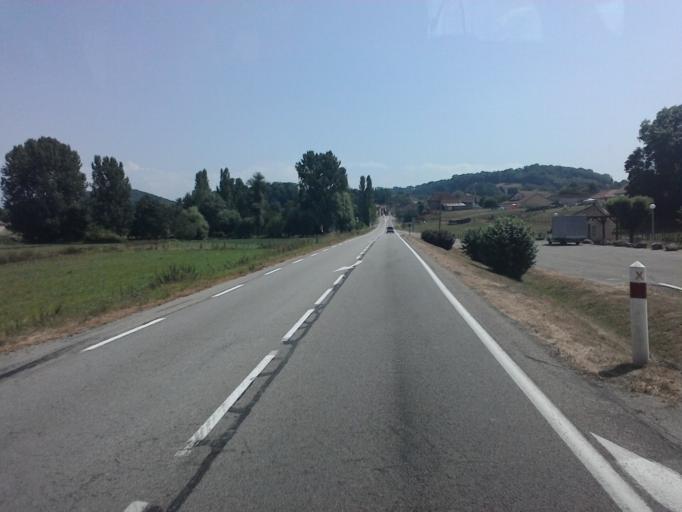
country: FR
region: Rhone-Alpes
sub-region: Departement de l'Isere
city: Les Abrets
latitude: 45.5171
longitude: 5.5958
